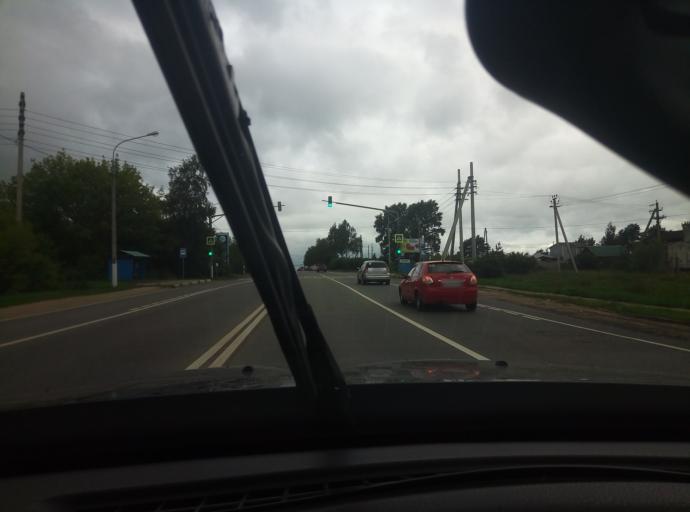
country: RU
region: Moskovskaya
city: Serpukhov
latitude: 54.9116
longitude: 37.4764
